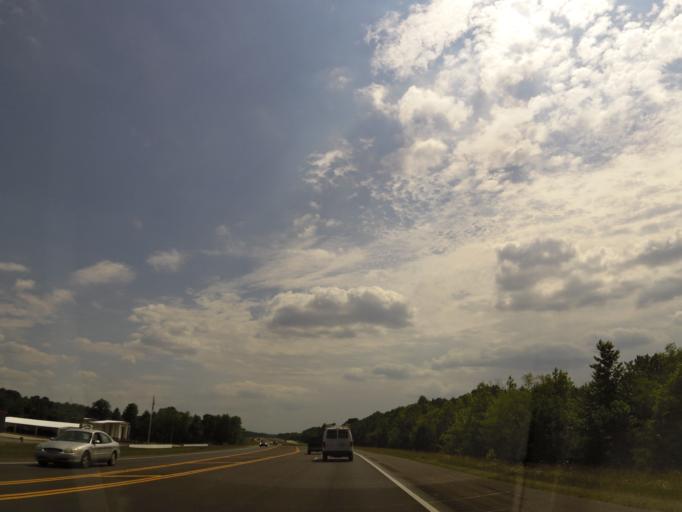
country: US
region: Tennessee
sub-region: Marion County
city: Jasper
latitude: 35.0802
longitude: -85.6094
